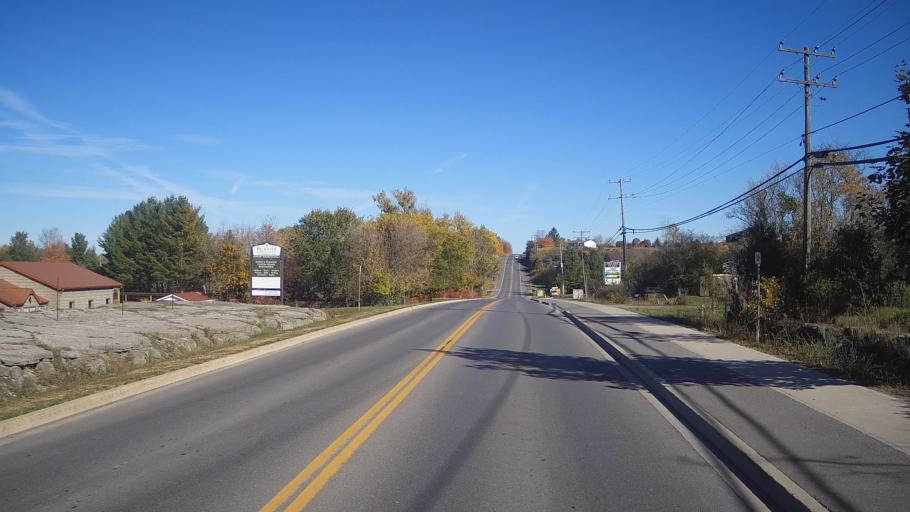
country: CA
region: Ontario
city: Kingston
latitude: 44.4071
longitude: -76.5916
